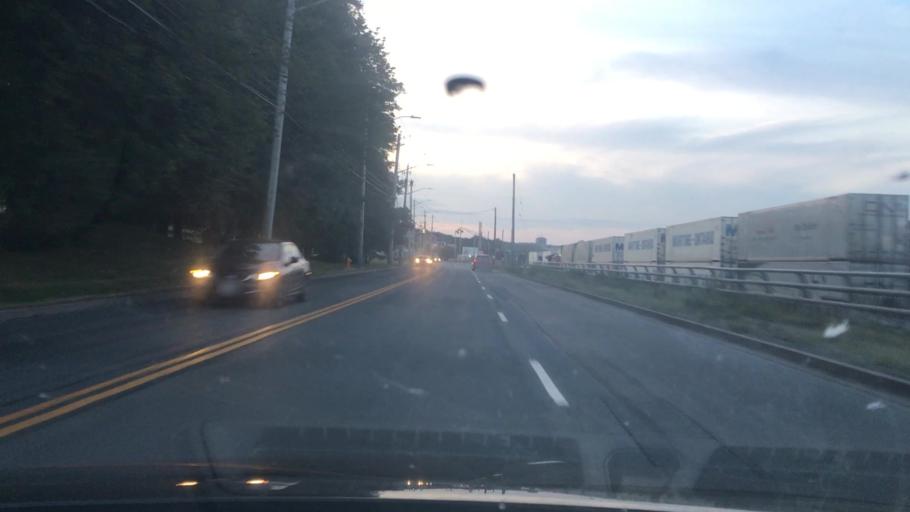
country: CA
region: Nova Scotia
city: Dartmouth
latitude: 44.6714
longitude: -63.6427
